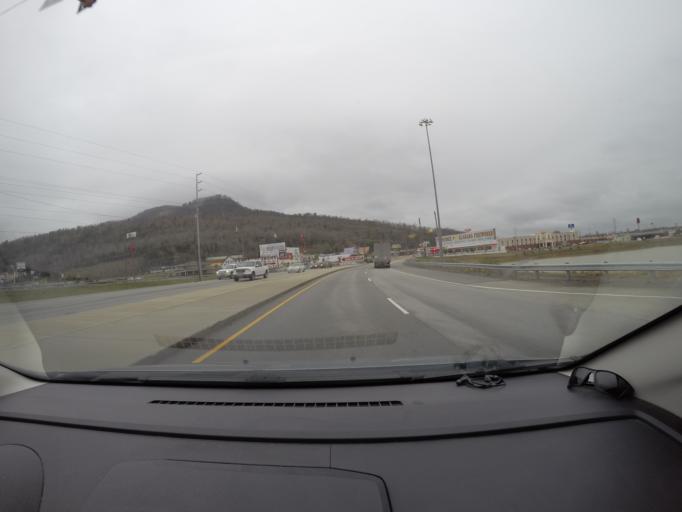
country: US
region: Tennessee
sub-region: Marion County
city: Kimball
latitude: 35.0411
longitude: -85.6898
